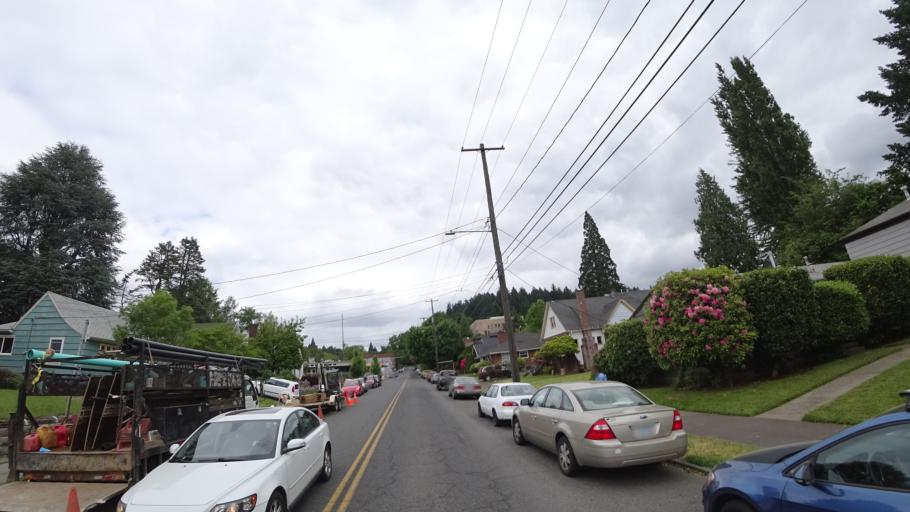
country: US
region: Oregon
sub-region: Multnomah County
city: Lents
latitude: 45.5168
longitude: -122.6040
